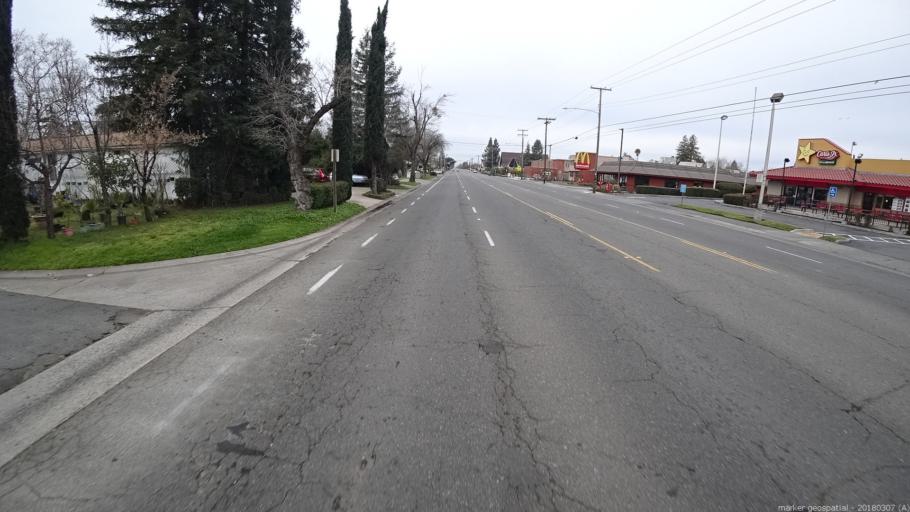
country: US
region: California
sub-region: Sacramento County
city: Arden-Arcade
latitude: 38.6176
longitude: -121.3663
